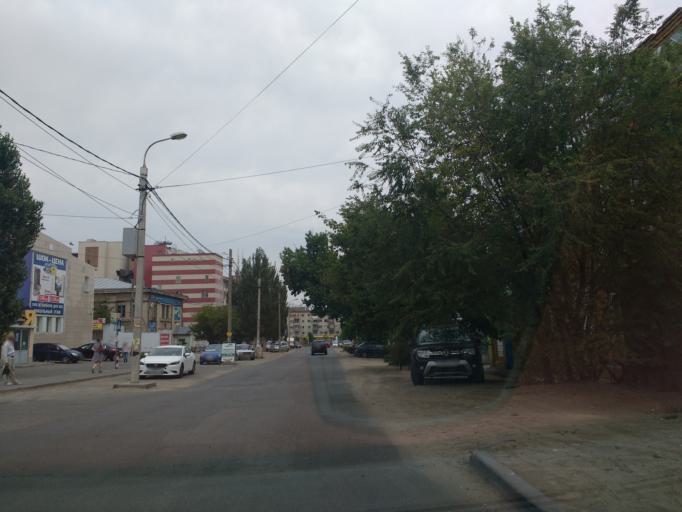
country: RU
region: Volgograd
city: Volgograd
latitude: 48.6900
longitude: 44.4832
